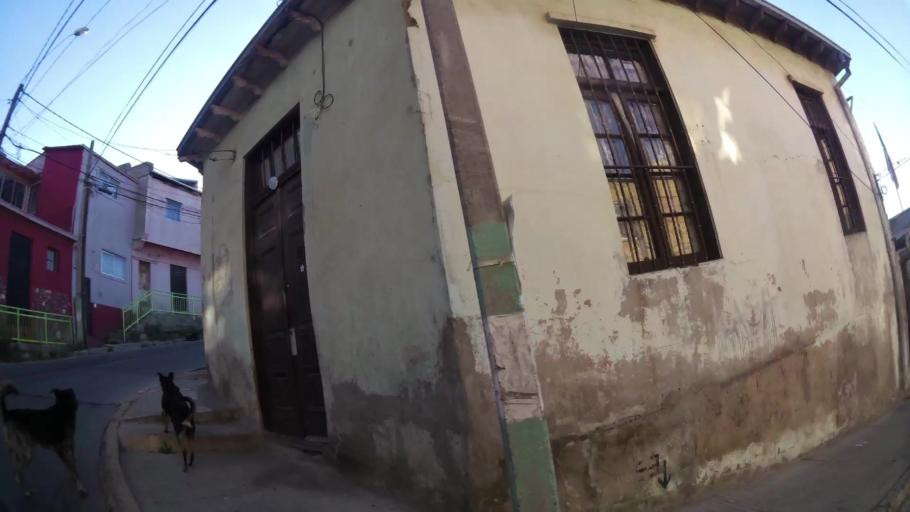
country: CL
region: Valparaiso
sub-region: Provincia de Valparaiso
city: Valparaiso
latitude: -33.0561
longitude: -71.6051
